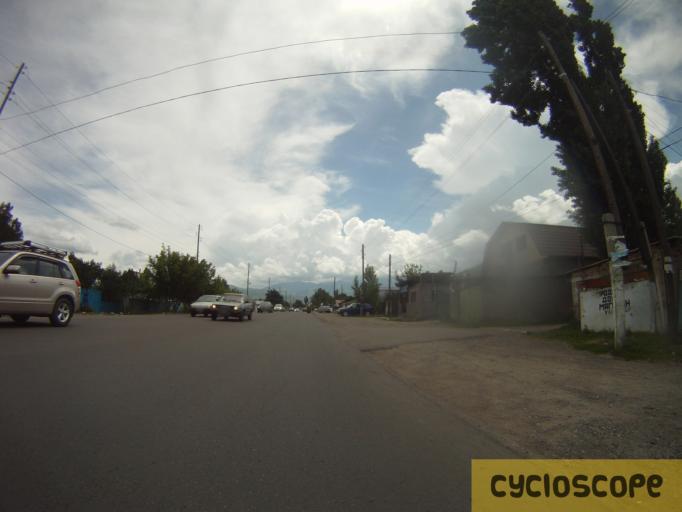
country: KZ
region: Almaty Oblysy
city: Esik
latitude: 43.3595
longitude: 77.4473
